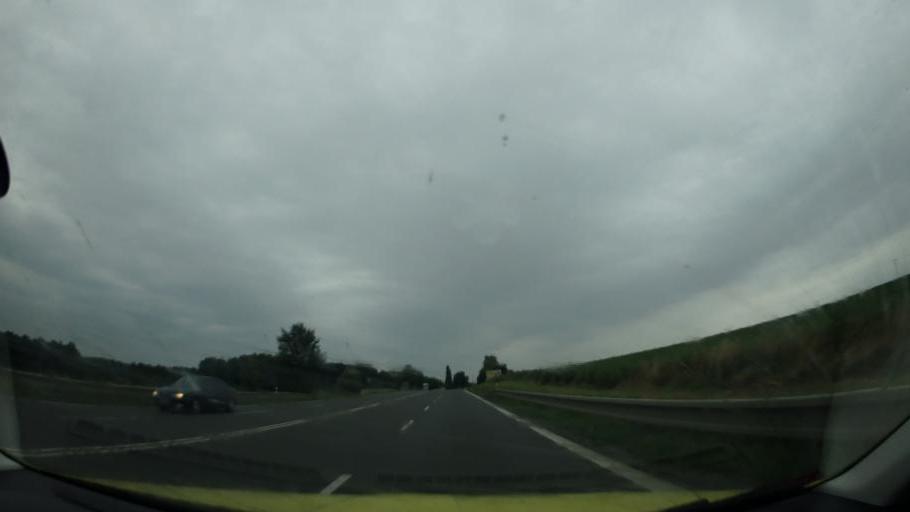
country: CZ
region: Olomoucky
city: Belotin
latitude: 49.5736
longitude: 17.7755
